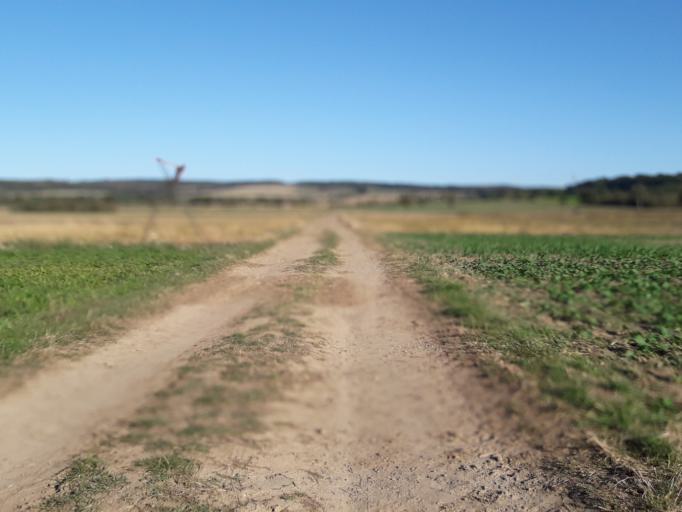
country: DE
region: North Rhine-Westphalia
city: Bad Lippspringe
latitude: 51.7627
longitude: 8.8293
